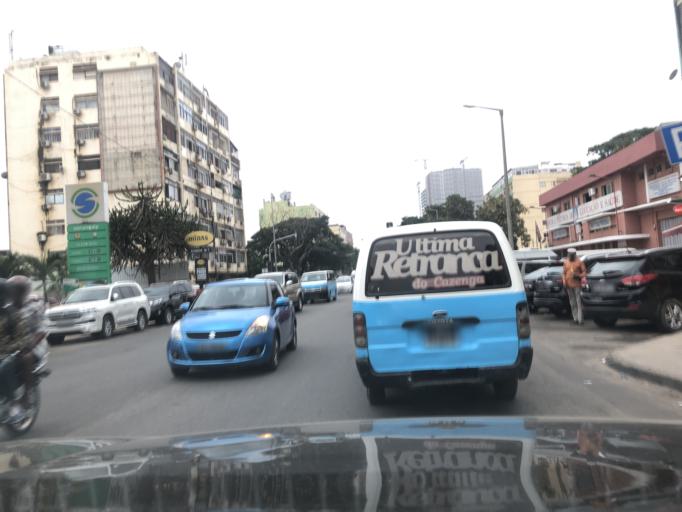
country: AO
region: Luanda
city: Luanda
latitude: -8.8221
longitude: 13.2505
